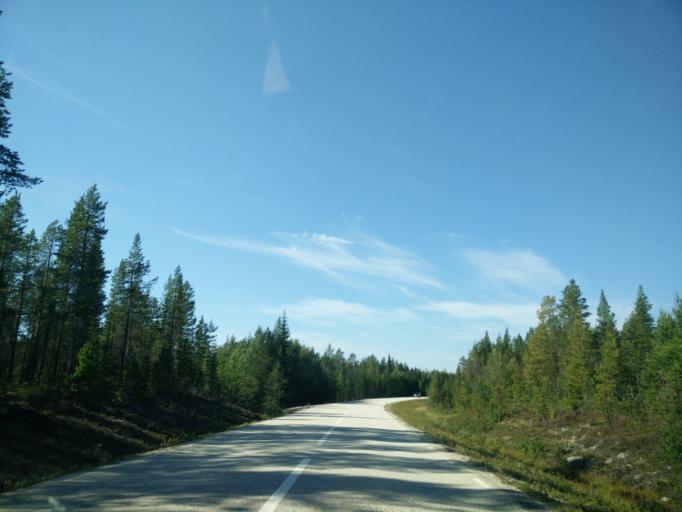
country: SE
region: Jaemtland
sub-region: Are Kommun
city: Jarpen
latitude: 62.8166
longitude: 13.5138
